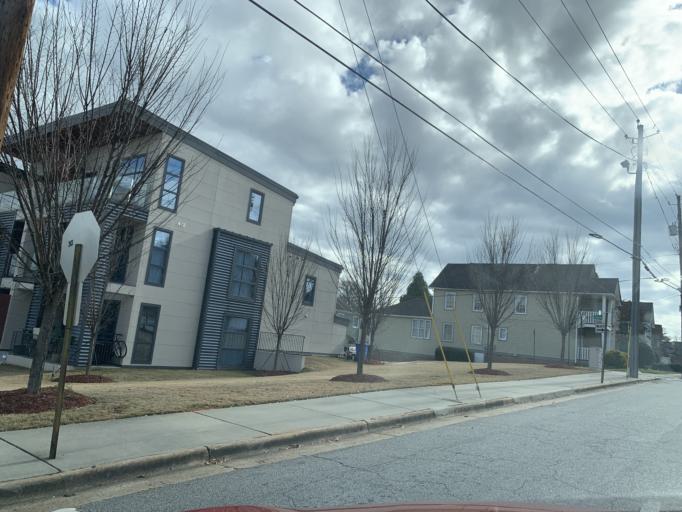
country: US
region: Georgia
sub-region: Fulton County
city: Atlanta
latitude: 33.7419
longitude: -84.3841
